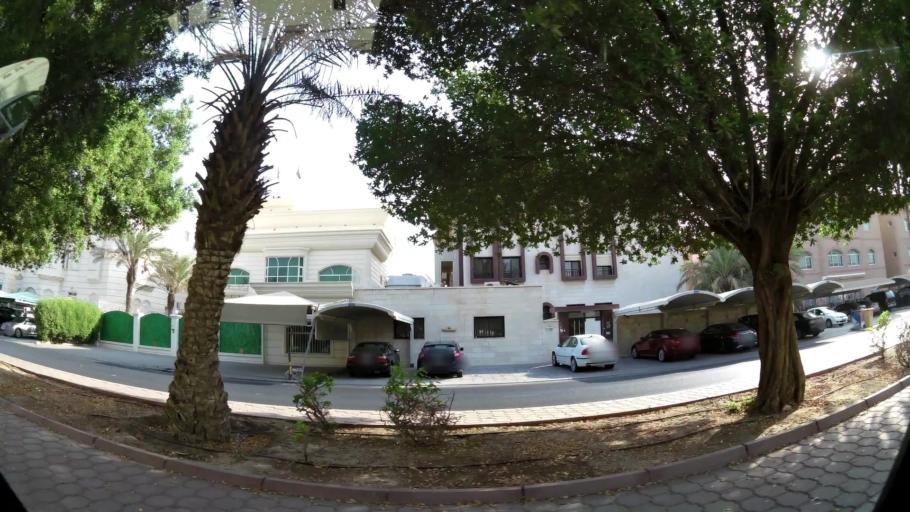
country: KW
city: Bayan
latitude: 29.3147
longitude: 48.0396
